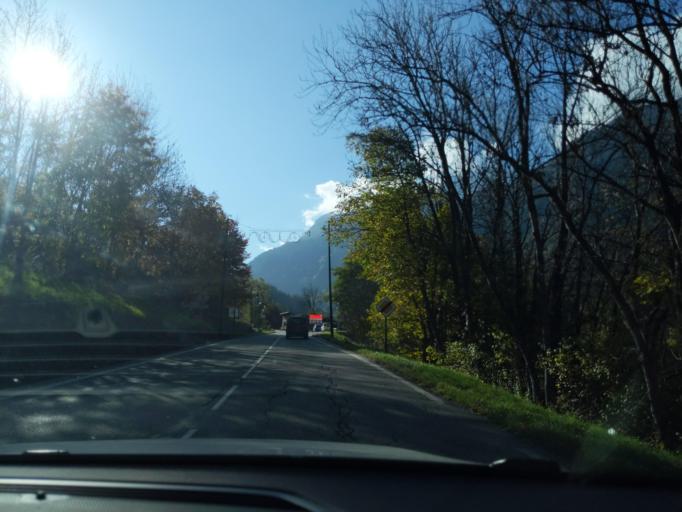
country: FR
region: Rhone-Alpes
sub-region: Departement de la Savoie
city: Seez
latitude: 45.5923
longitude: 6.8825
